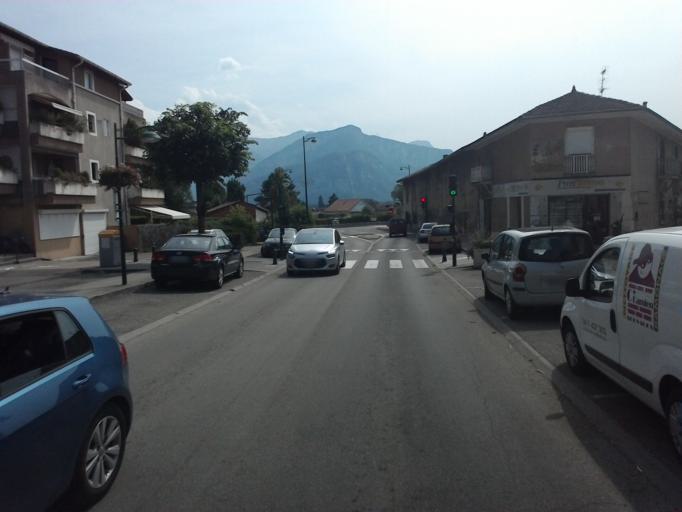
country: FR
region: Rhone-Alpes
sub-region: Departement de l'Isere
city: La Buisse
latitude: 45.3344
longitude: 5.6211
